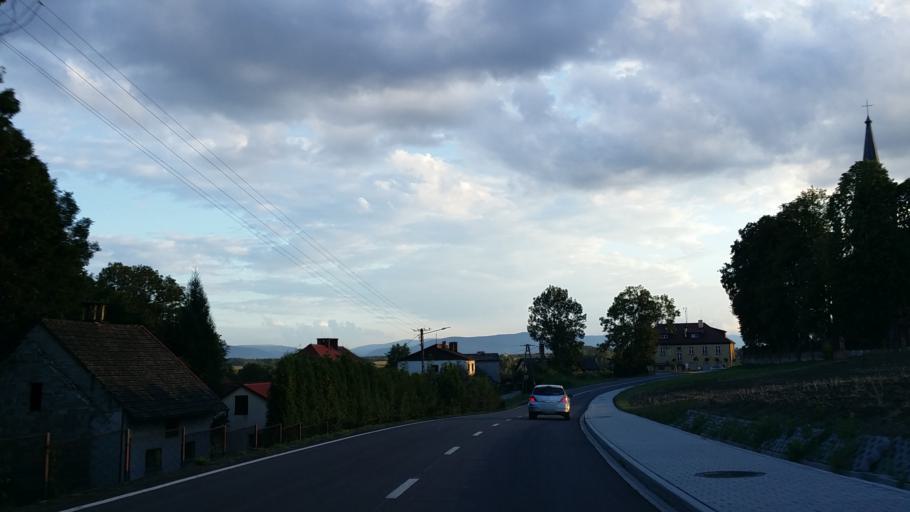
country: PL
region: Lesser Poland Voivodeship
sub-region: Powiat oswiecimski
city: Osiek
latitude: 49.9550
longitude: 19.2691
